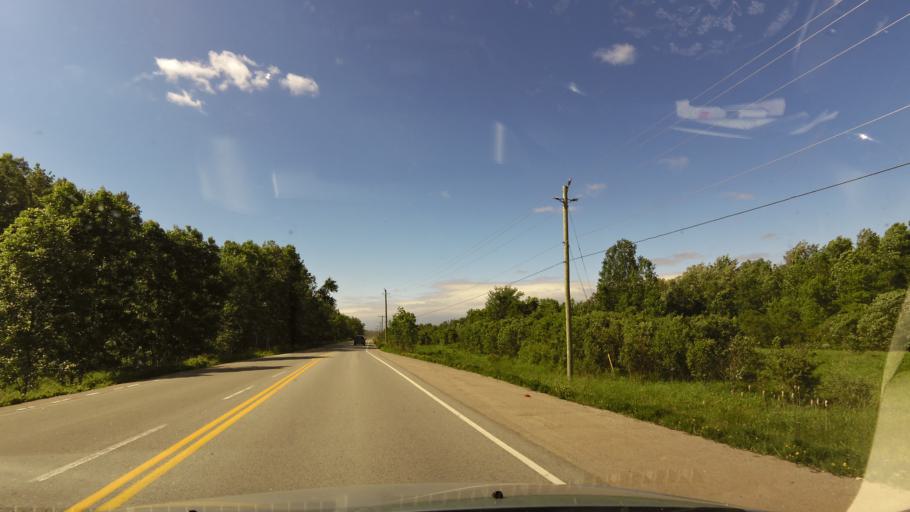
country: CA
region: Ontario
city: Bradford West Gwillimbury
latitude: 44.2083
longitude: -79.6274
